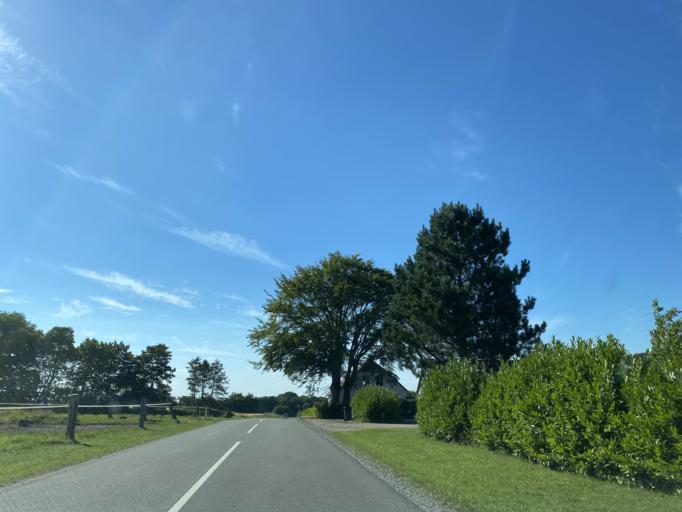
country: DK
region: South Denmark
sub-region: Vejle Kommune
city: Give
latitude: 55.8928
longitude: 9.2804
